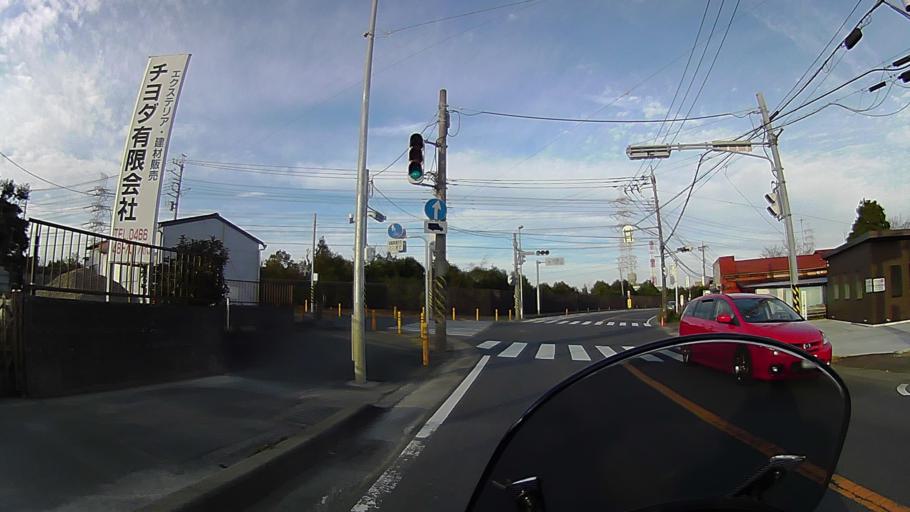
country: JP
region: Kanagawa
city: Atsugi
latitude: 35.4175
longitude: 139.4189
